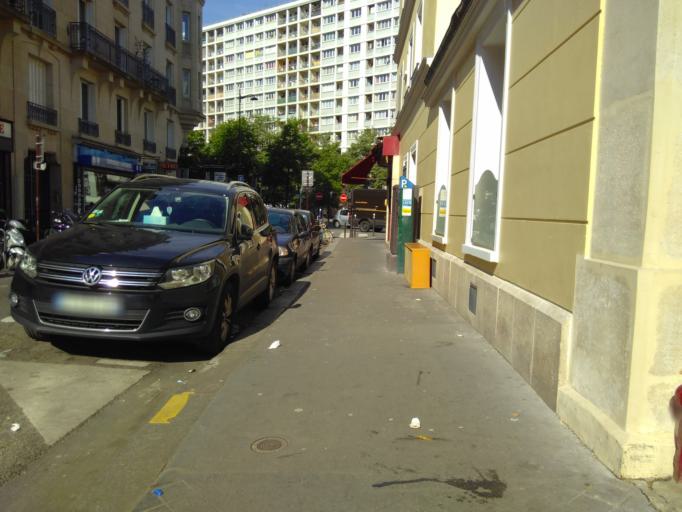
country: FR
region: Ile-de-France
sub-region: Departement de Seine-Saint-Denis
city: Le Pre-Saint-Gervais
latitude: 48.8879
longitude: 2.3744
